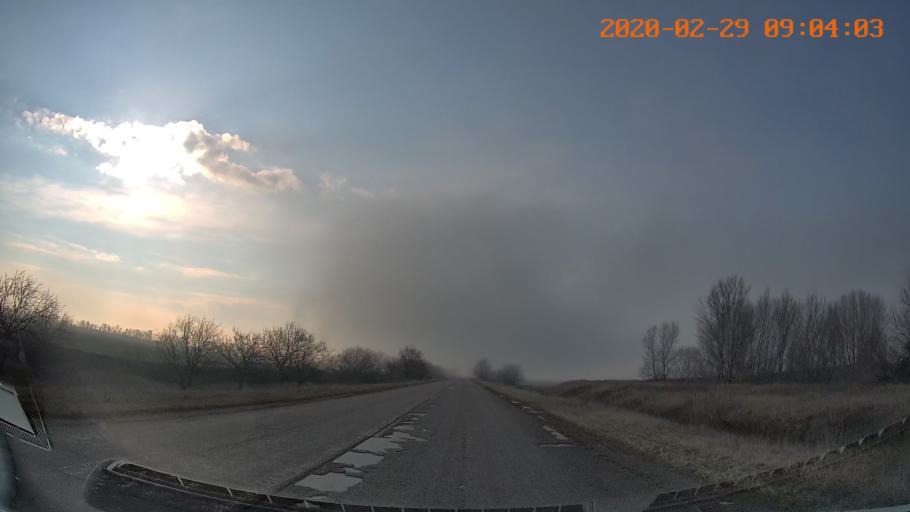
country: UA
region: Odessa
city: Velykoploske
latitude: 46.9079
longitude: 29.7344
